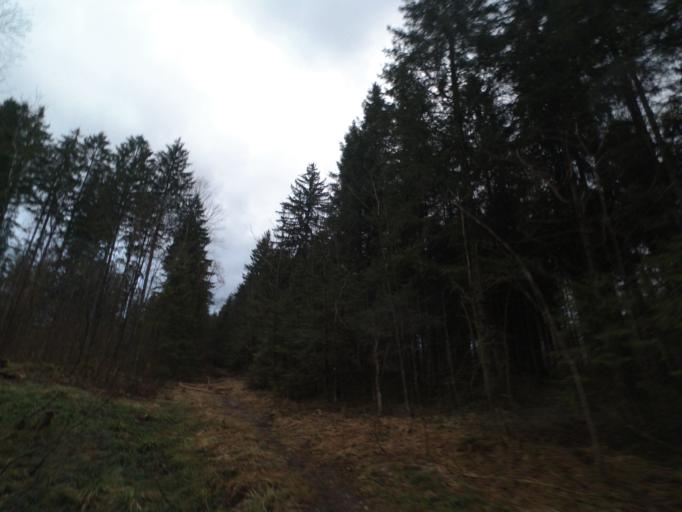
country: AT
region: Salzburg
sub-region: Politischer Bezirk Salzburg-Umgebung
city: Elsbethen
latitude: 47.7378
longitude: 13.0805
